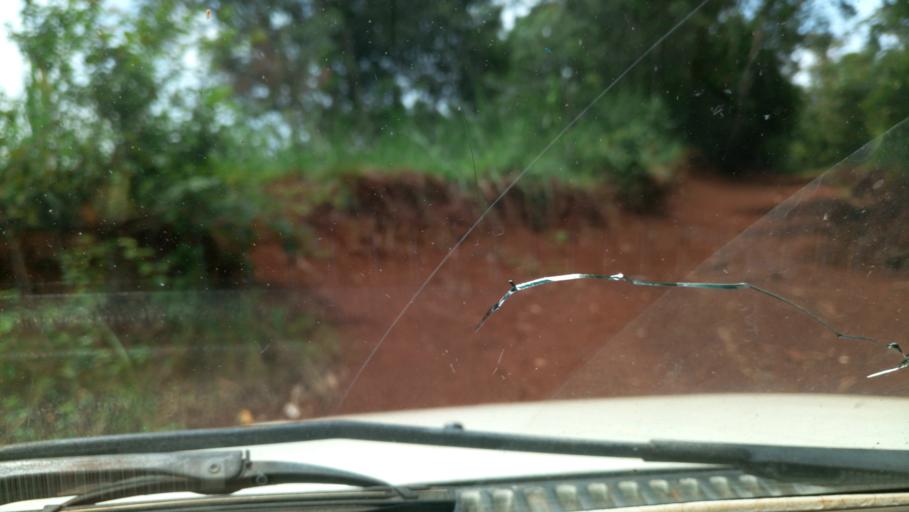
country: KE
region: Nyeri
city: Othaya
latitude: -0.5877
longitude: 37.0124
